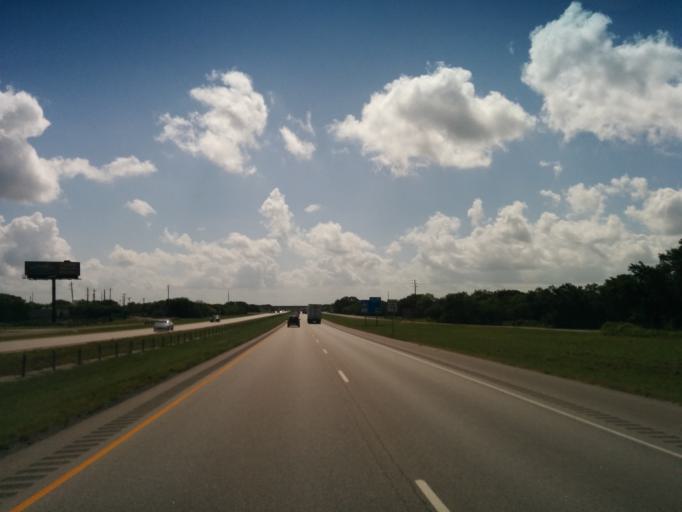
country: US
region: Texas
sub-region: Colorado County
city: Columbus
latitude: 29.6935
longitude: -96.5818
